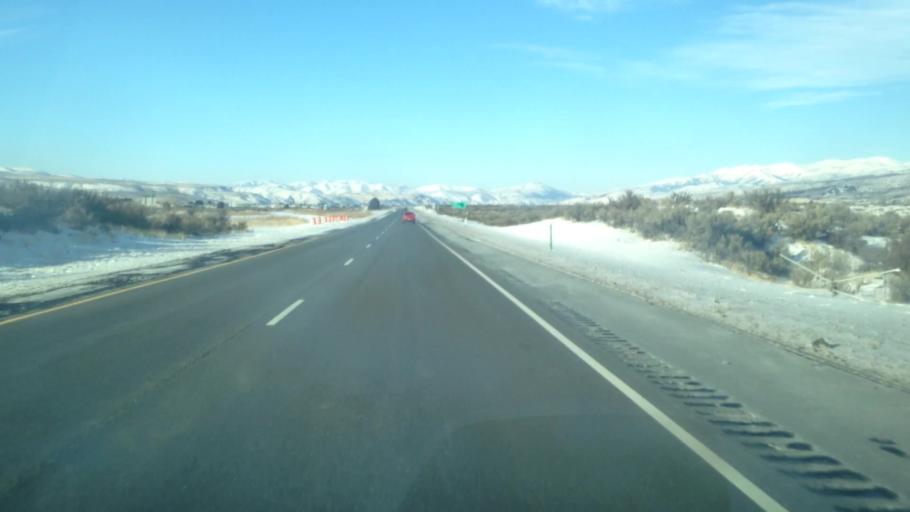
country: US
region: Idaho
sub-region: Bannock County
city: Pocatello
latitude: 42.6699
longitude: -112.2139
